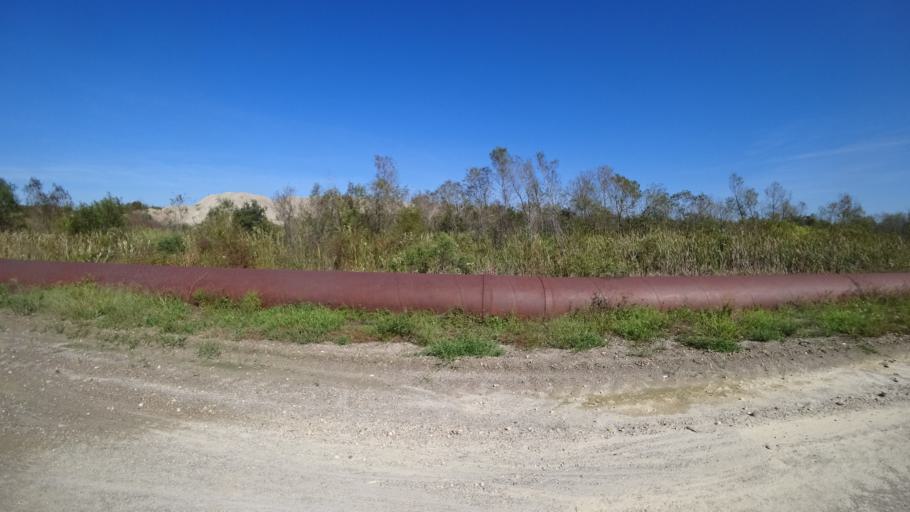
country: US
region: Florida
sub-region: Hillsborough County
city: Balm
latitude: 27.6493
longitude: -82.0869
